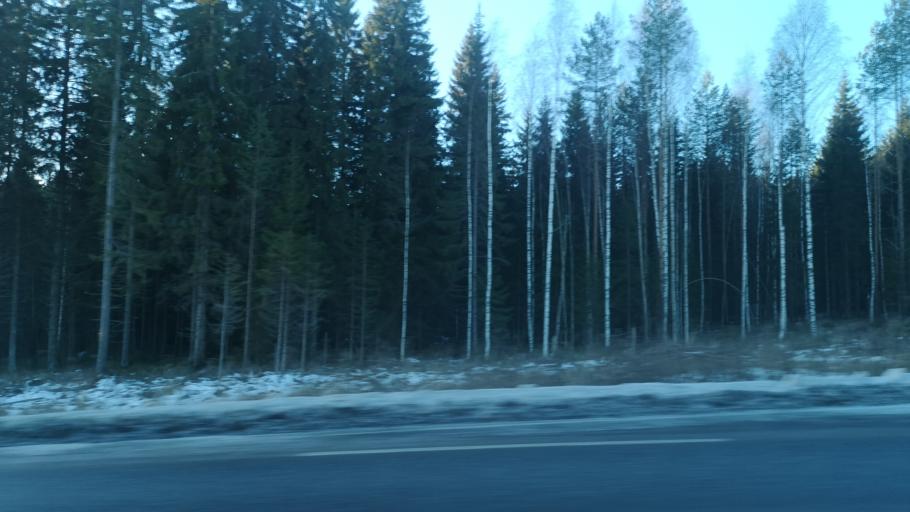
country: FI
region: Southern Savonia
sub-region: Pieksaemaeki
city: Juva
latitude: 61.7931
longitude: 27.5978
